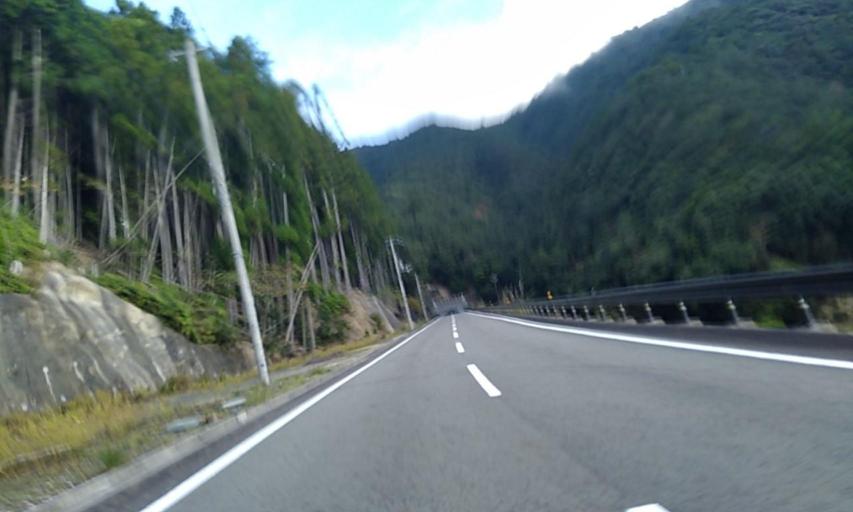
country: JP
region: Wakayama
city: Shingu
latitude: 33.8785
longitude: 135.8762
